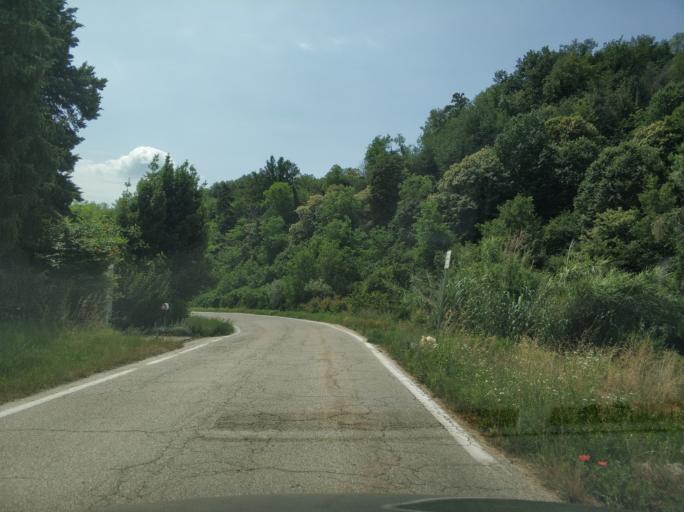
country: IT
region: Piedmont
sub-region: Provincia di Cuneo
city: Santo Stefano Roero
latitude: 44.7855
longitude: 7.9558
